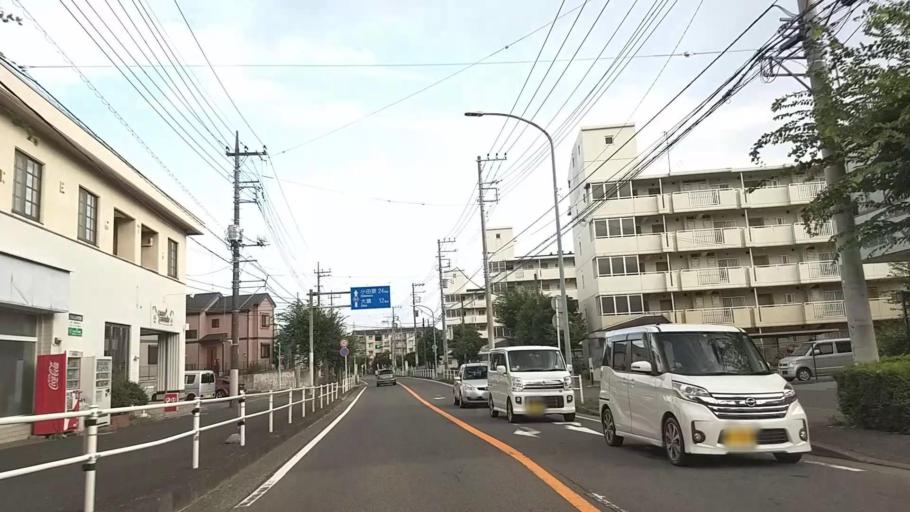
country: JP
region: Kanagawa
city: Isehara
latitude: 35.3981
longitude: 139.2994
